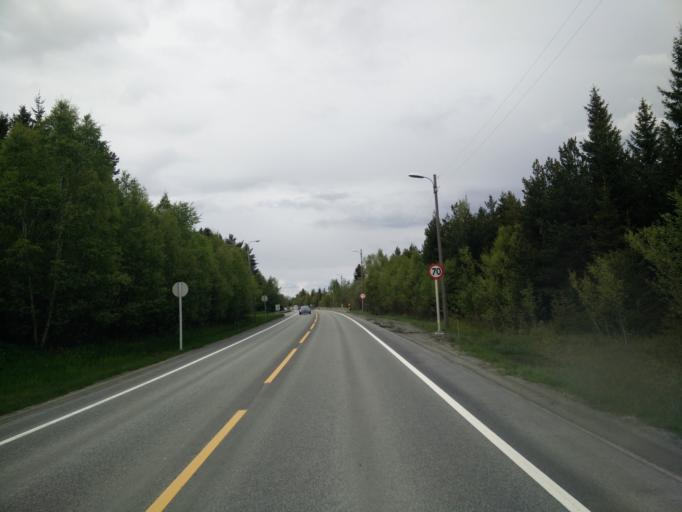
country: NO
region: Sor-Trondelag
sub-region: Trondheim
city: Trondheim
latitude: 63.3459
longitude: 10.3685
